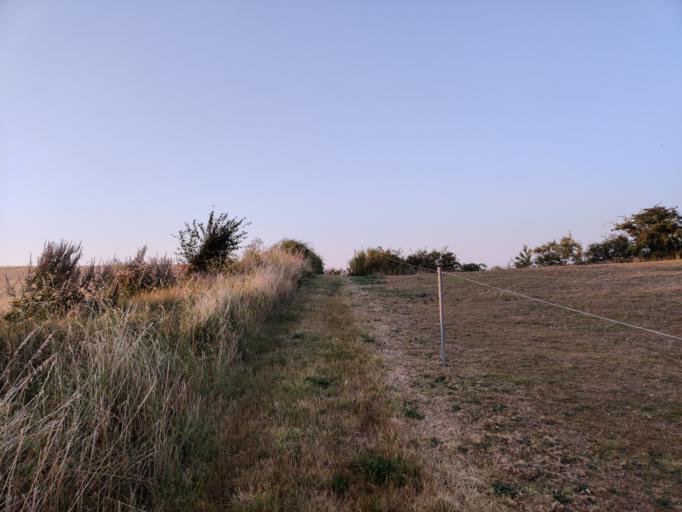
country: DK
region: South Denmark
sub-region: AEro Kommune
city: AEroskobing
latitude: 54.8986
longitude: 10.3116
